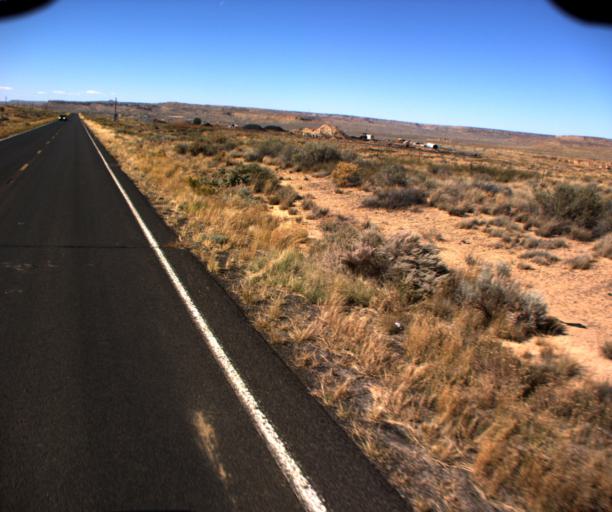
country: US
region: Arizona
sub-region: Navajo County
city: First Mesa
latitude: 35.8729
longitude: -110.5604
